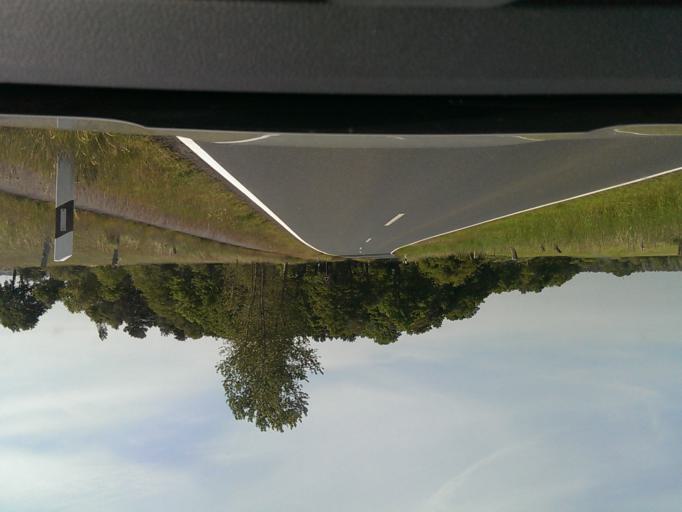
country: DE
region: Lower Saxony
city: Wietze
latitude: 52.6664
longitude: 9.7716
